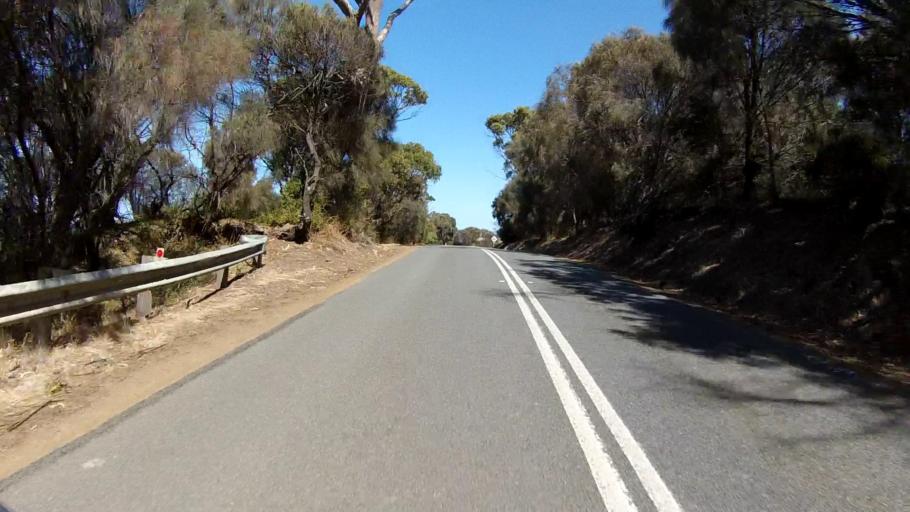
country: AU
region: Tasmania
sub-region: Sorell
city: Sorell
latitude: -42.2409
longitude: 148.0124
